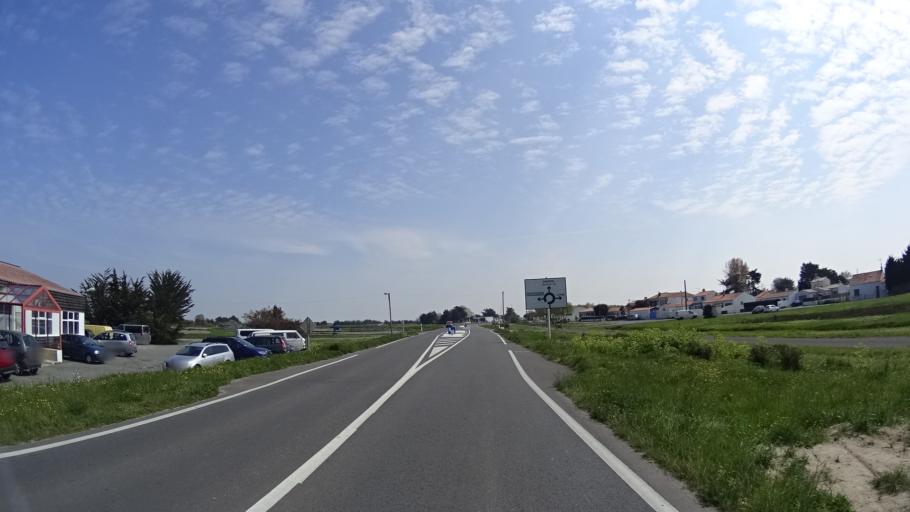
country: FR
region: Pays de la Loire
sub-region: Departement de la Vendee
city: La Gueriniere
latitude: 46.9831
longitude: -2.2673
